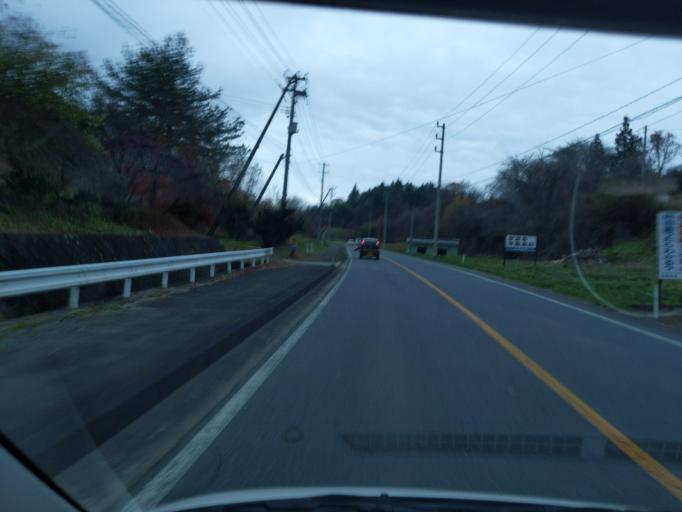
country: JP
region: Iwate
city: Ichinoseki
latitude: 39.0152
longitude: 141.3288
